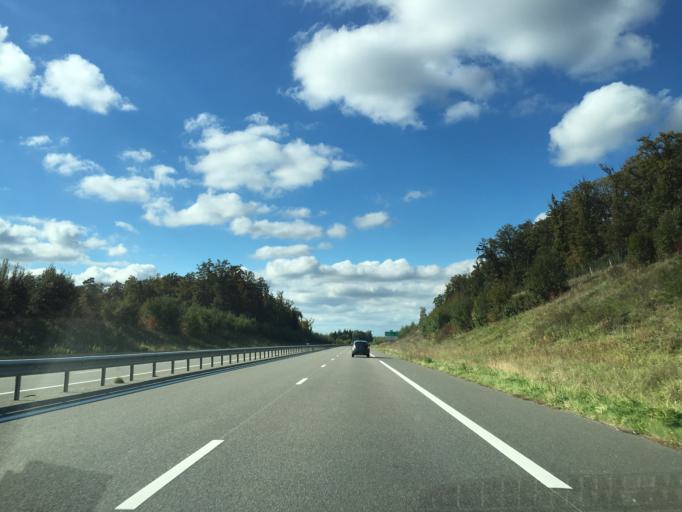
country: FR
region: Lorraine
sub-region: Departement de Meurthe-et-Moselle
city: Baccarat
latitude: 48.5030
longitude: 6.6825
